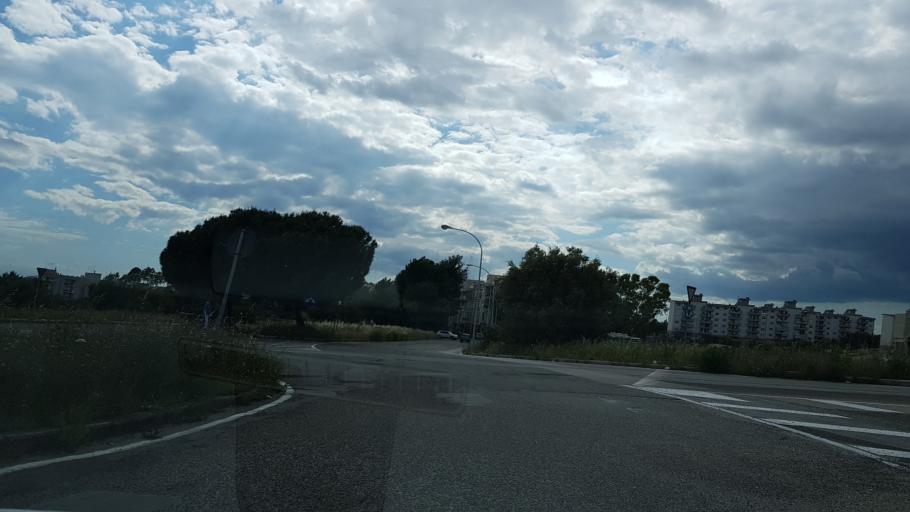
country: IT
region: Apulia
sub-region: Provincia di Taranto
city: Paolo VI
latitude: 40.5273
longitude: 17.2769
